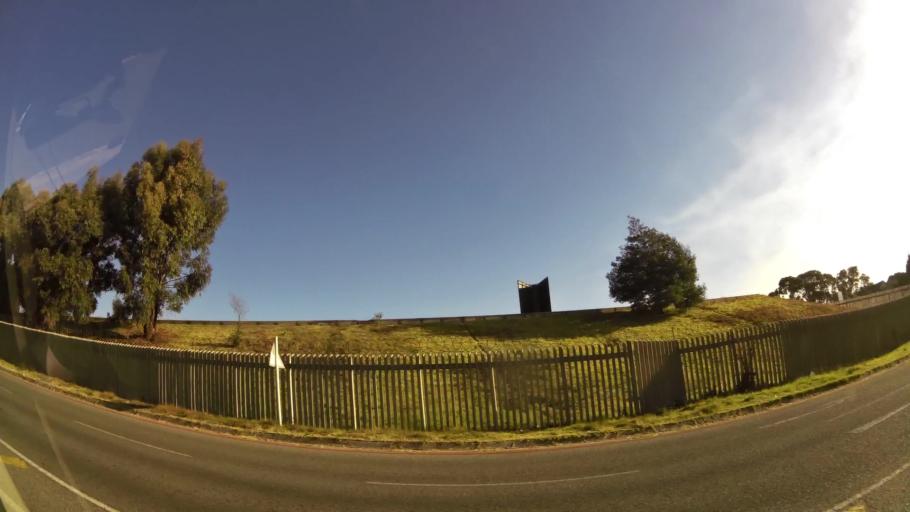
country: ZA
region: Gauteng
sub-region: City of Johannesburg Metropolitan Municipality
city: Roodepoort
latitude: -26.1362
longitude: 27.8631
